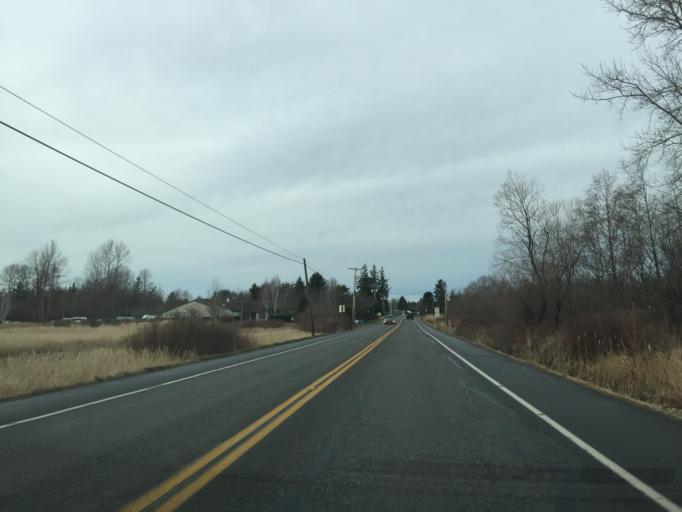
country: US
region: Washington
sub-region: Whatcom County
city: Marietta-Alderwood
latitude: 48.8287
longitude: -122.5373
